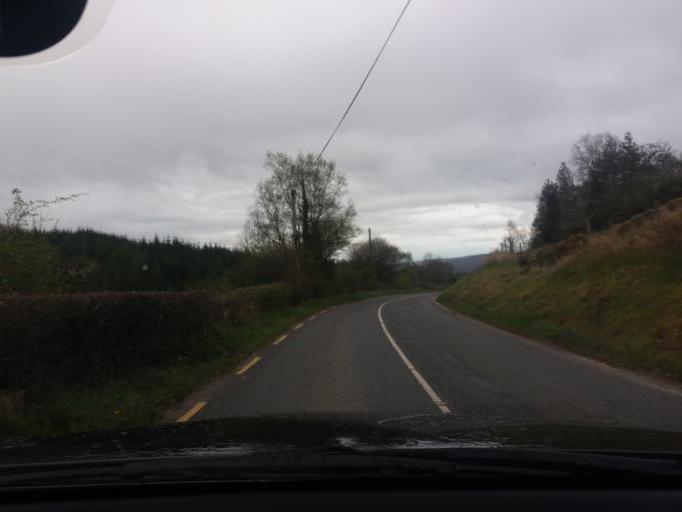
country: IE
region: Ulster
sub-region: An Cabhan
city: Ballyconnell
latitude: 54.1573
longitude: -7.7628
